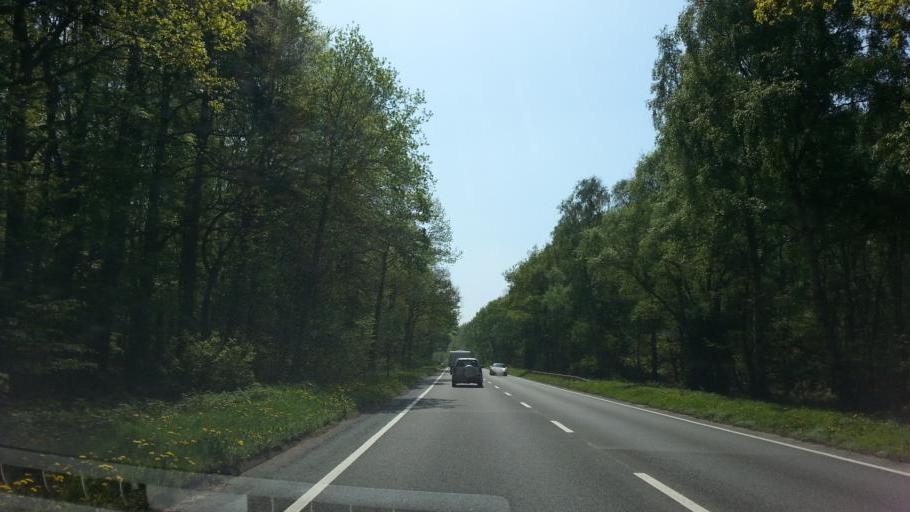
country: GB
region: England
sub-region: Nottinghamshire
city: Babworth
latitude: 53.2944
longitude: -1.0331
